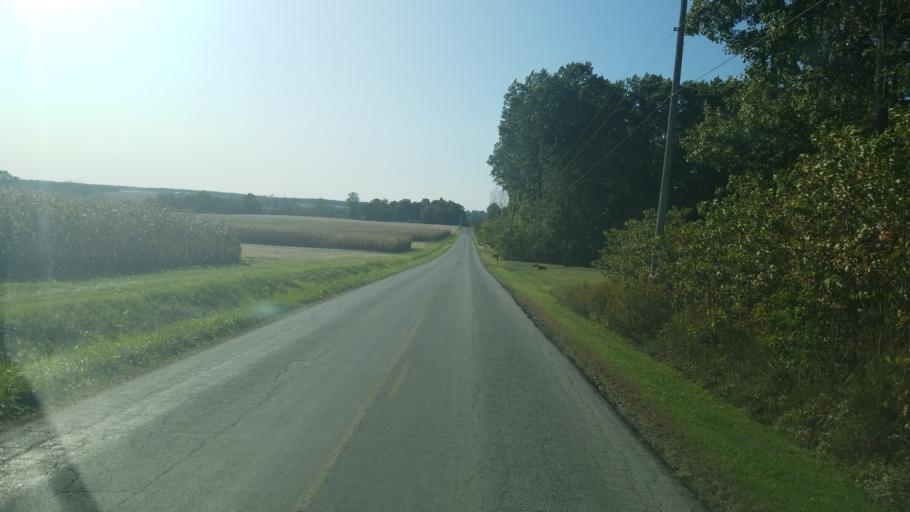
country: US
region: Ohio
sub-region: Wayne County
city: West Salem
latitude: 40.8582
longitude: -82.1201
